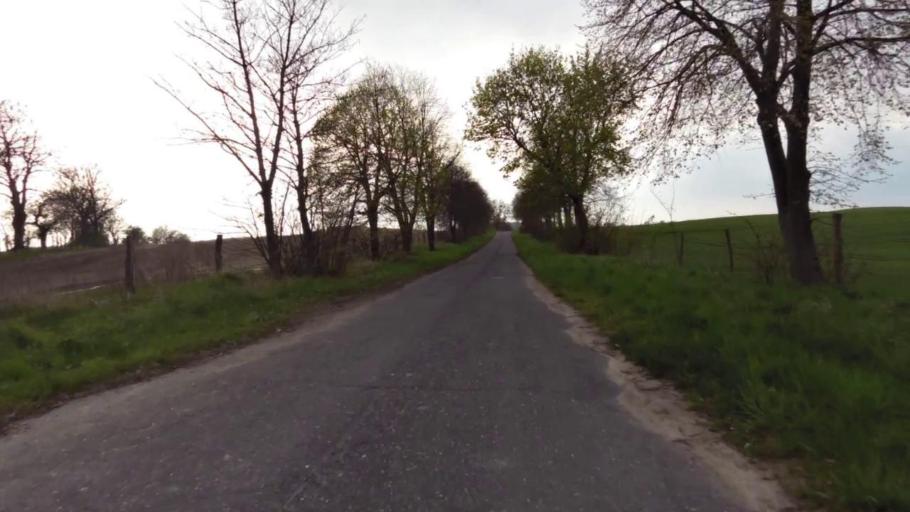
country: PL
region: West Pomeranian Voivodeship
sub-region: Powiat mysliborski
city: Mysliborz
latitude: 52.8911
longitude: 14.7884
